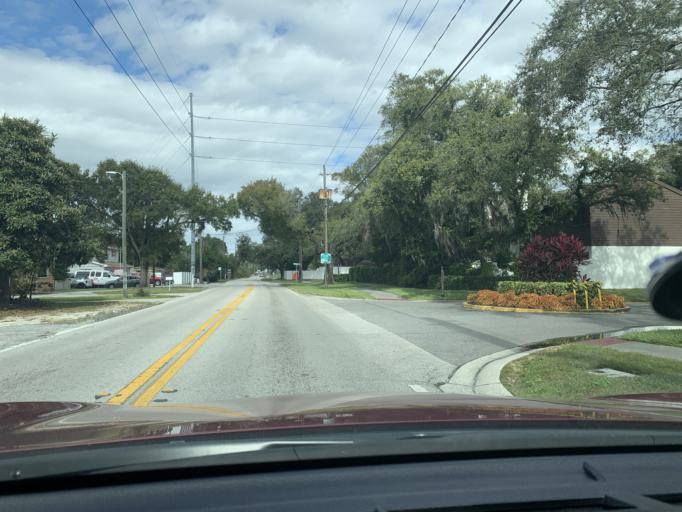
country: US
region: Florida
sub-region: Hillsborough County
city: Egypt Lake-Leto
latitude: 28.0210
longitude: -82.5007
